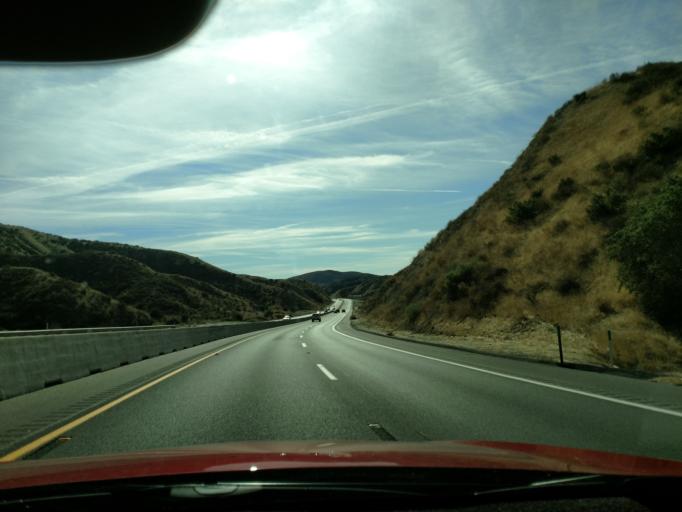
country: US
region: California
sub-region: Riverside County
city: Beaumont
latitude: 33.8942
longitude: -116.9876
